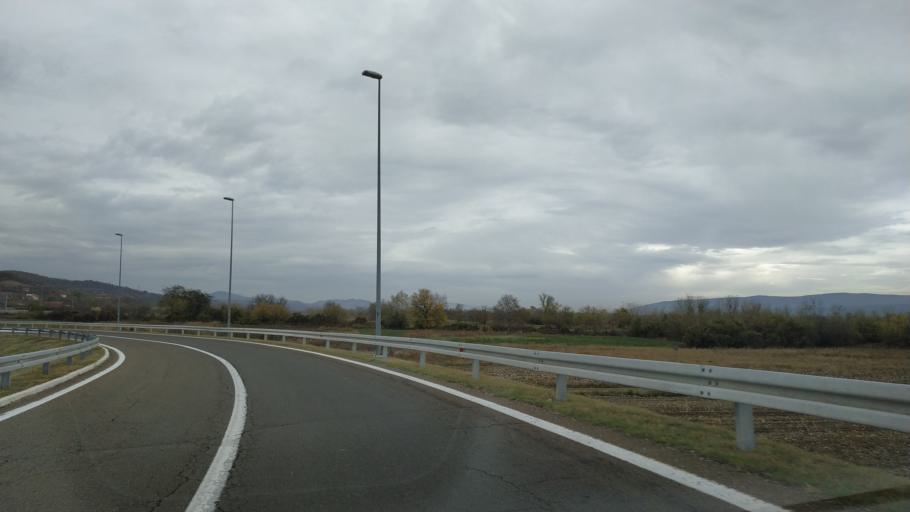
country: RS
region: Central Serbia
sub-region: Nisavski Okrug
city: Aleksinac
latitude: 43.5221
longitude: 21.7293
